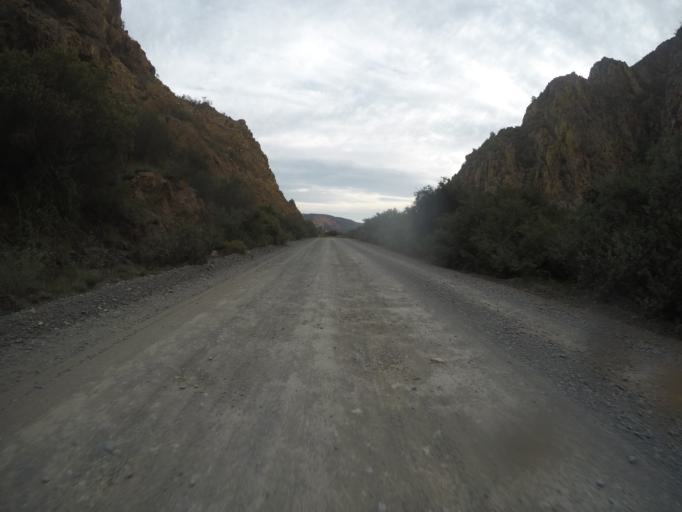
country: ZA
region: Eastern Cape
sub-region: Cacadu District Municipality
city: Willowmore
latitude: -33.5191
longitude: 23.6749
